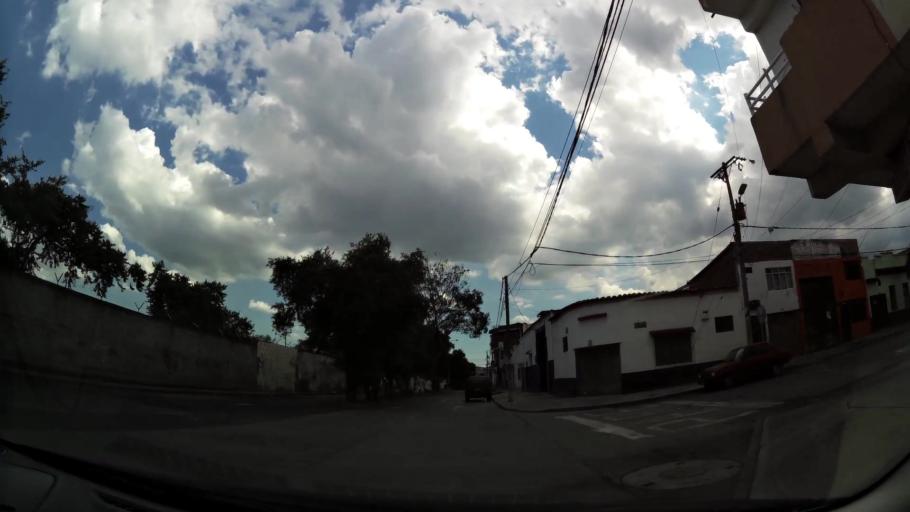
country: CO
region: Valle del Cauca
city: Cali
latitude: 3.4403
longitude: -76.5307
